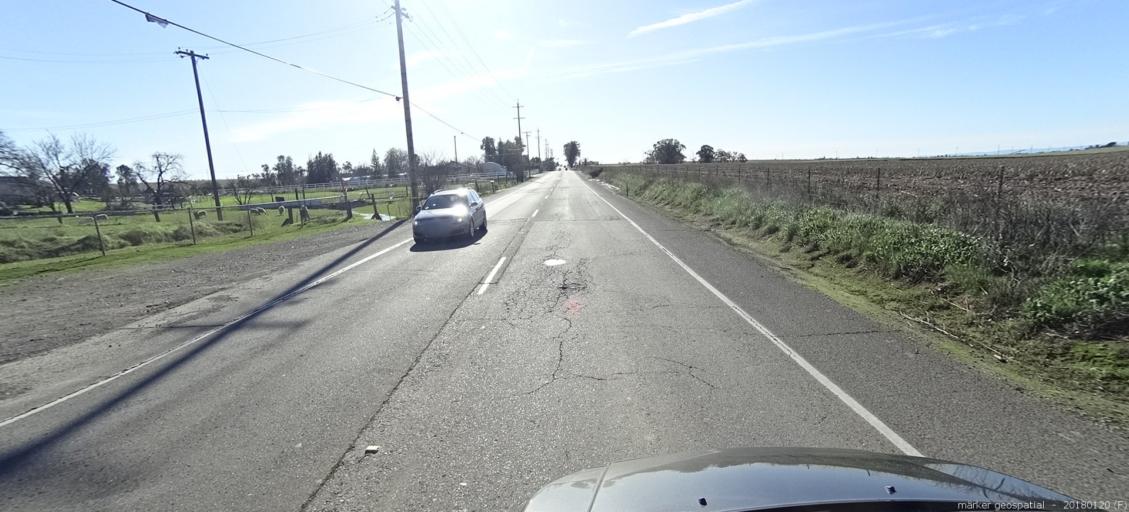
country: US
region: California
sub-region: Sacramento County
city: Wilton
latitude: 38.5057
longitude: -121.2191
